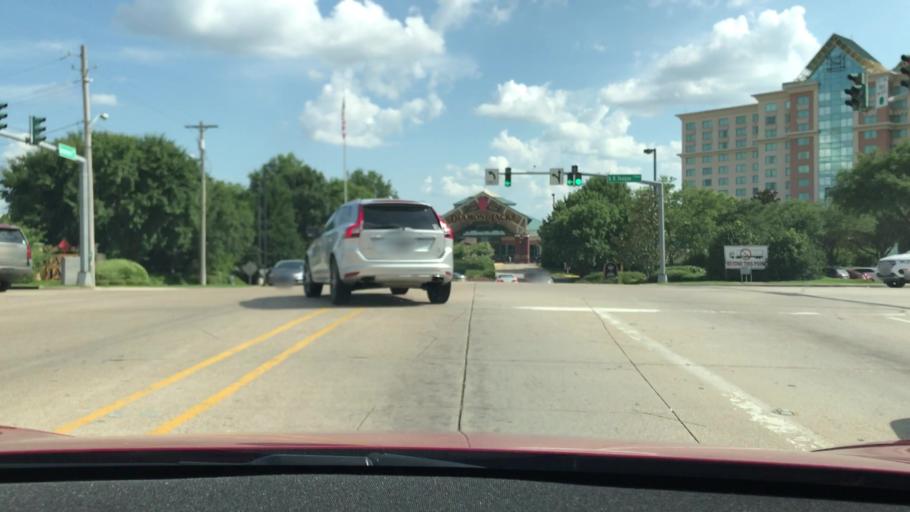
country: US
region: Louisiana
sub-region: Bossier Parish
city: Bossier City
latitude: 32.5121
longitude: -93.7268
